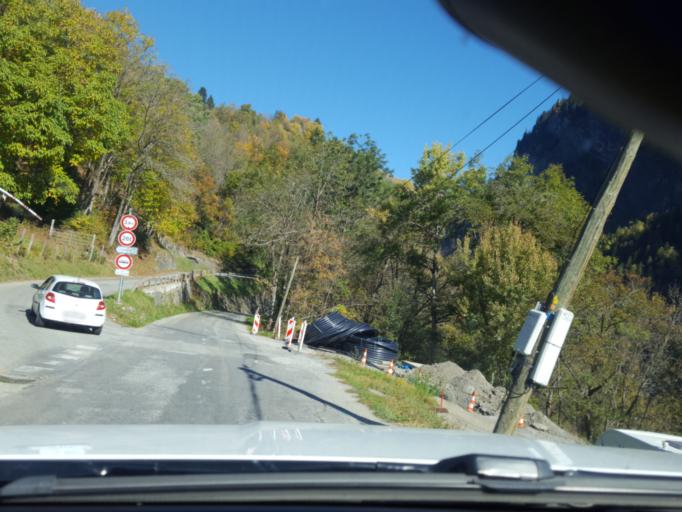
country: FR
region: Rhone-Alpes
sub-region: Departement de la Savoie
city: Seez
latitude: 45.6312
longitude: 6.7843
